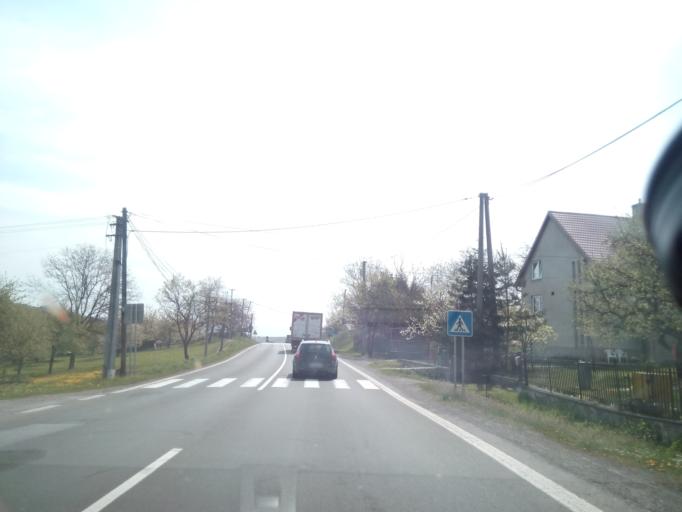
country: SK
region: Presovsky
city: Giraltovce
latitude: 49.0365
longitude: 21.4593
